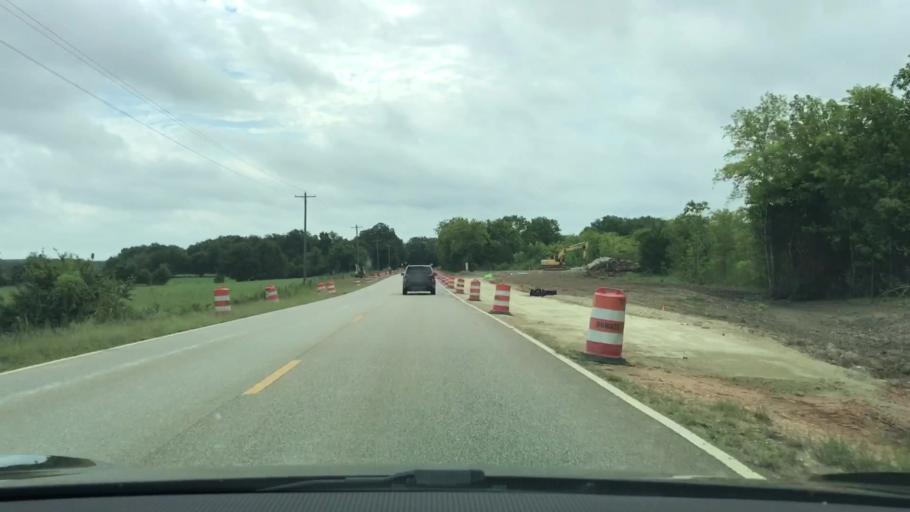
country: US
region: Alabama
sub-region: Montgomery County
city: Pike Road
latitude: 32.2866
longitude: -86.0811
